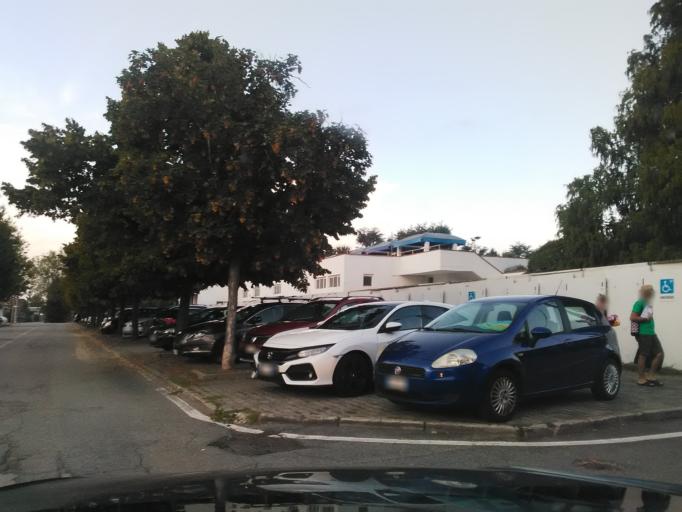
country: IT
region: Piedmont
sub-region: Provincia di Vercelli
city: Cigliano
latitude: 45.3096
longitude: 8.0300
